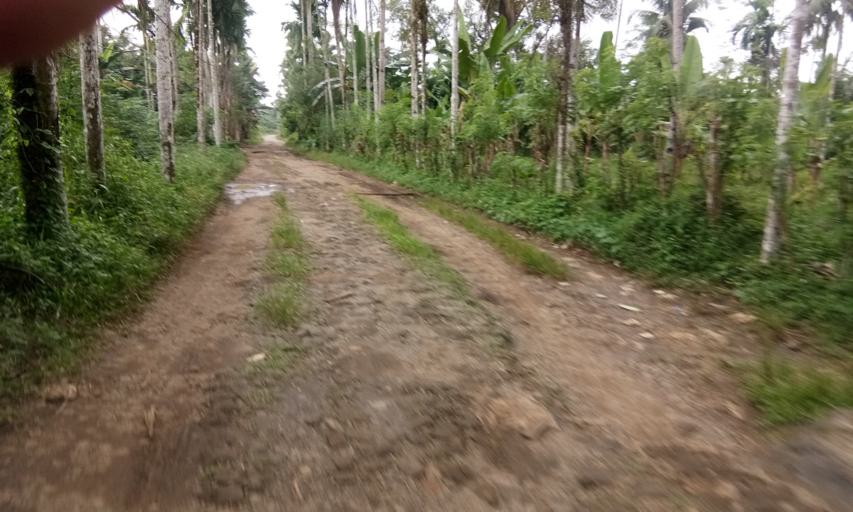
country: ID
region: North Sumatra
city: Deli Tua
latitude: 3.4707
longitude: 98.6107
